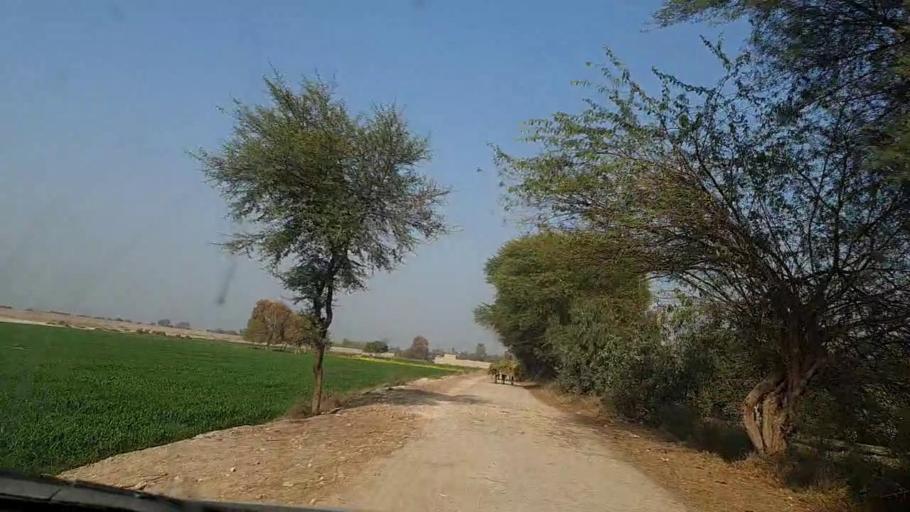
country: PK
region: Sindh
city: Moro
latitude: 26.7980
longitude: 67.9446
